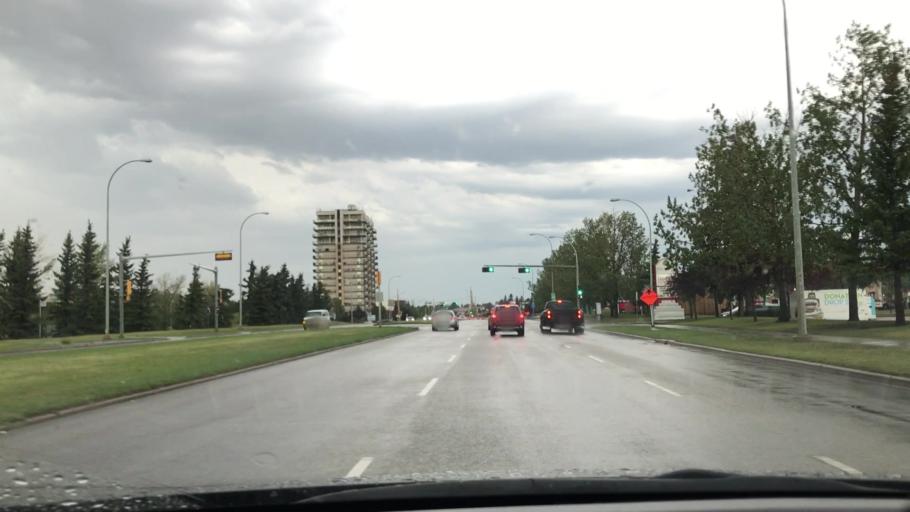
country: CA
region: Alberta
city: Edmonton
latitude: 53.4555
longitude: -113.4344
